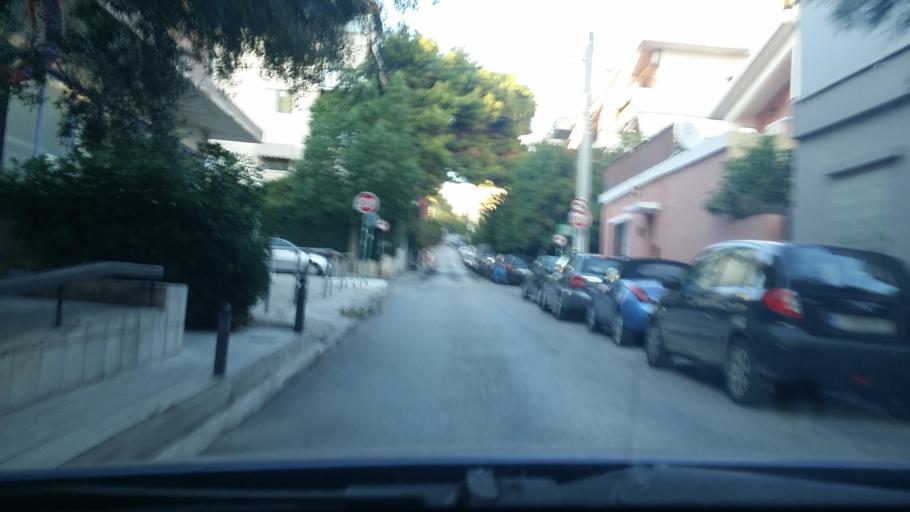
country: GR
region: Attica
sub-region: Nomarchia Athinas
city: Irakleio
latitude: 38.0481
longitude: 23.7568
